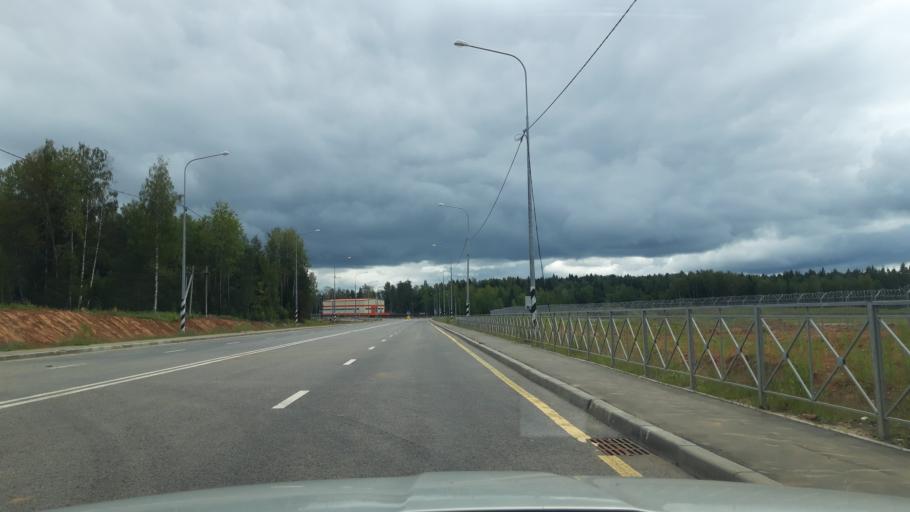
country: RU
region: Moskovskaya
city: Lozhki
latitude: 56.0826
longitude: 37.0875
